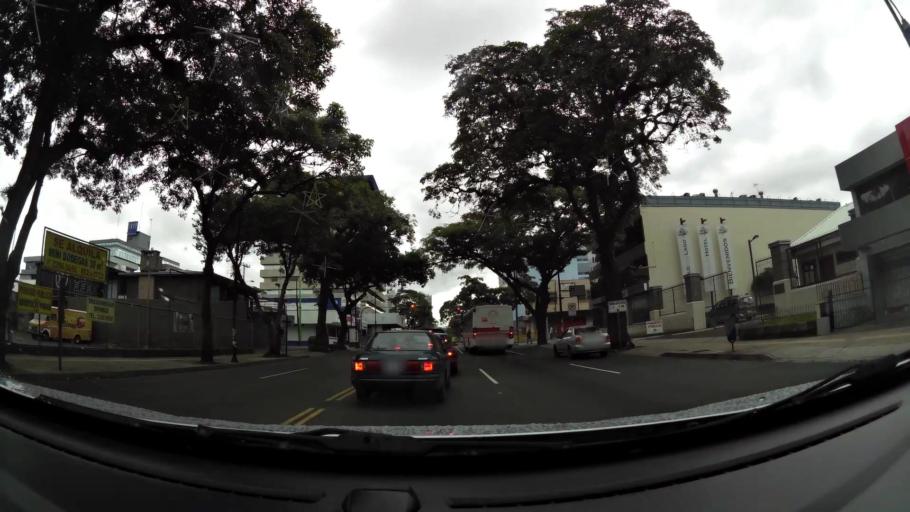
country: CR
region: San Jose
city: San Jose
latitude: 9.9358
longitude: -84.0976
